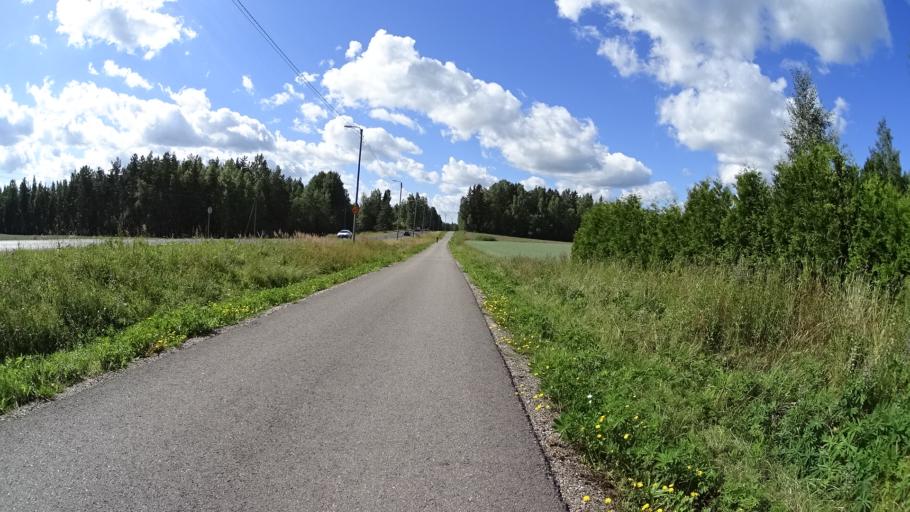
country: FI
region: Uusimaa
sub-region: Helsinki
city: Jaervenpaeae
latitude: 60.4376
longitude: 25.0680
